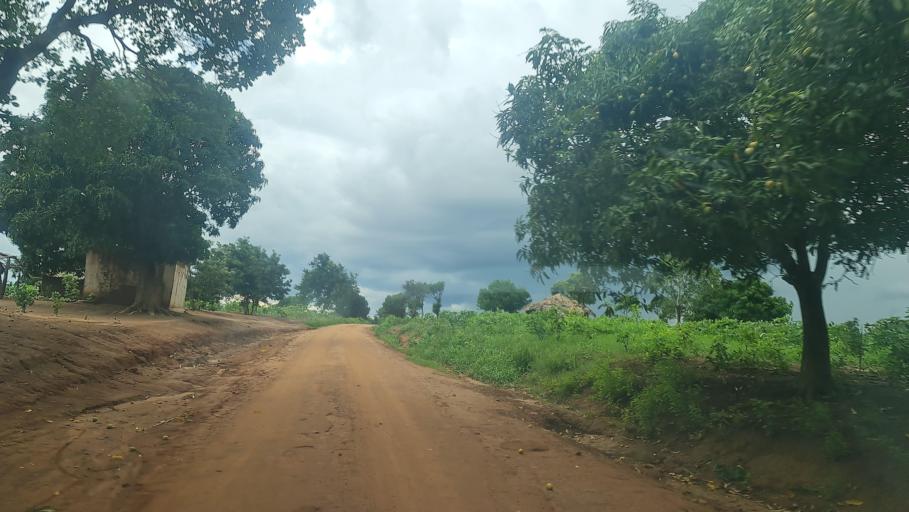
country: MW
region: Southern Region
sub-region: Nsanje District
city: Nsanje
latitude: -17.3887
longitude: 35.5754
